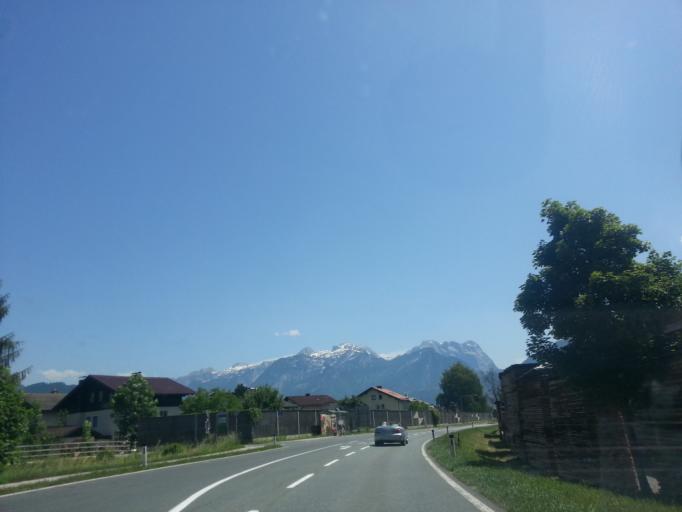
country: AT
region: Salzburg
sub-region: Politischer Bezirk Hallein
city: Kuchl
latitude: 47.6397
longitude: 13.1375
